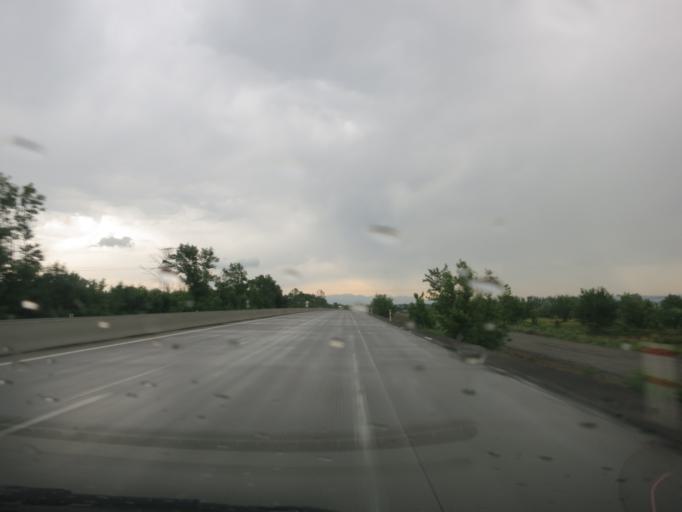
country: GE
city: Agara
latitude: 42.0568
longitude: 43.8688
